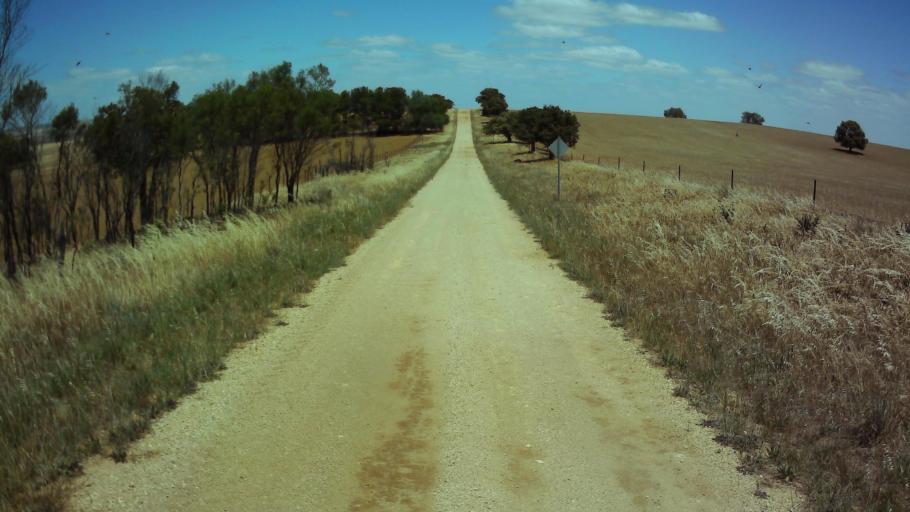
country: AU
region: New South Wales
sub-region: Weddin
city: Grenfell
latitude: -33.9545
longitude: 148.3657
